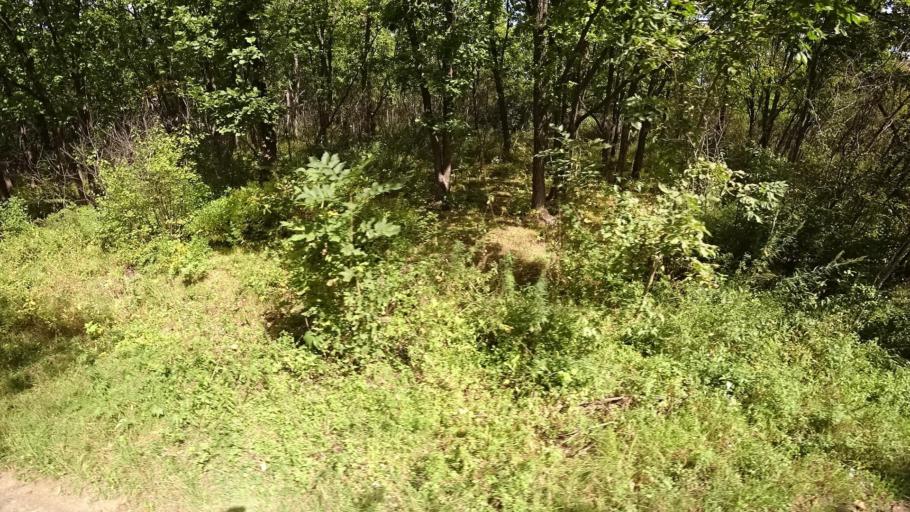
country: RU
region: Primorskiy
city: Yakovlevka
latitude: 44.6498
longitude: 133.5902
